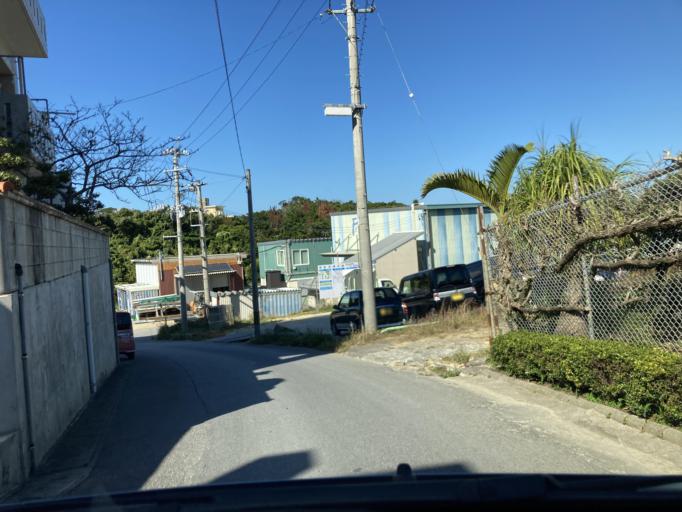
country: JP
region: Okinawa
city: Gushikawa
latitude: 26.3669
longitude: 127.8286
